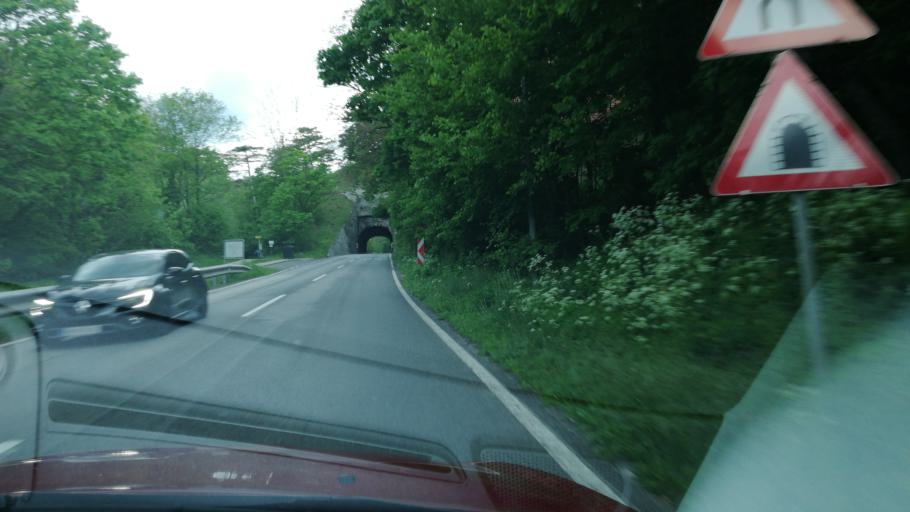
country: AT
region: Lower Austria
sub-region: Politischer Bezirk Baden
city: Baden
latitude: 48.0152
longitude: 16.1980
